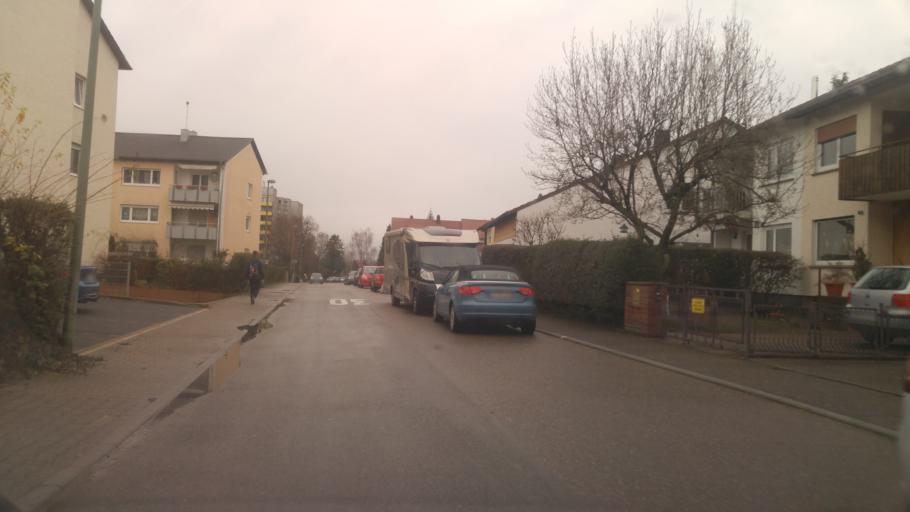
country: DE
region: Baden-Wuerttemberg
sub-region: Regierungsbezirk Stuttgart
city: Gerlingen
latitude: 48.8060
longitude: 9.0827
